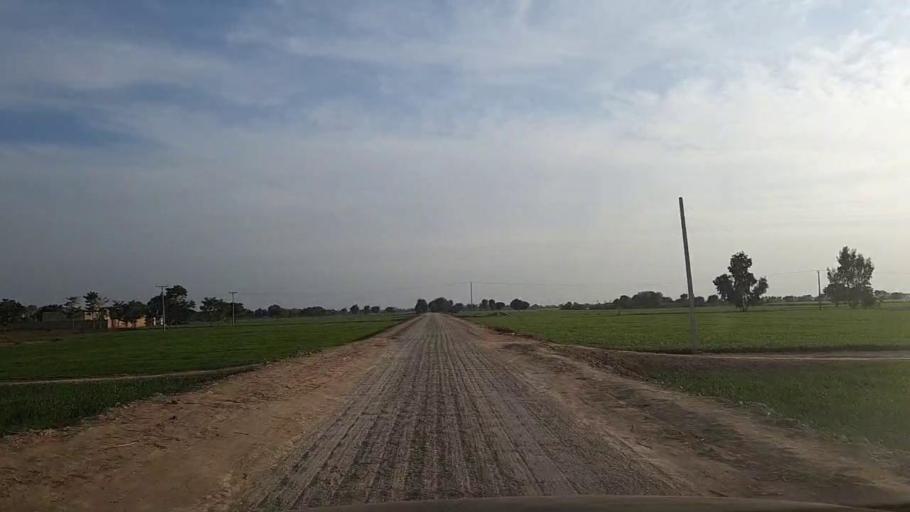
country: PK
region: Sindh
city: Jam Sahib
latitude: 26.4440
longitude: 68.5717
